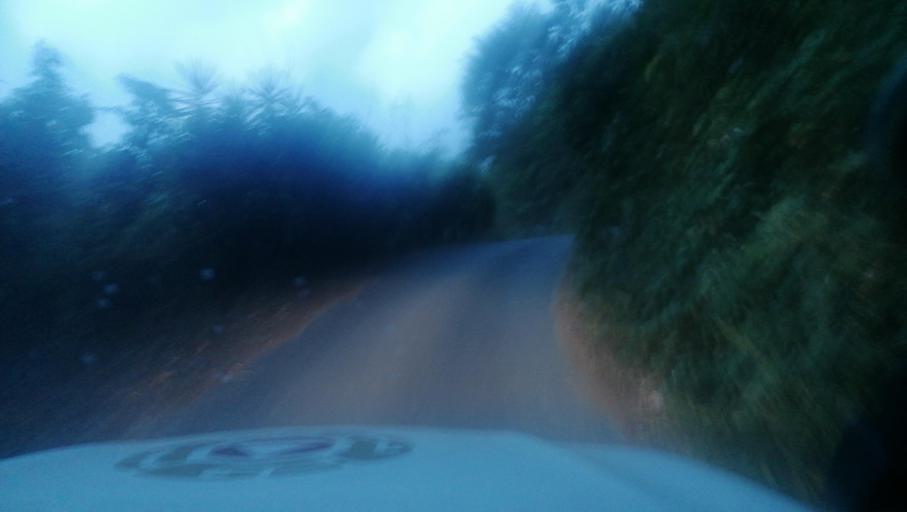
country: MX
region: Chiapas
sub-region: Cacahoatan
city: Benito Juarez
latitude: 15.1254
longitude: -92.2088
